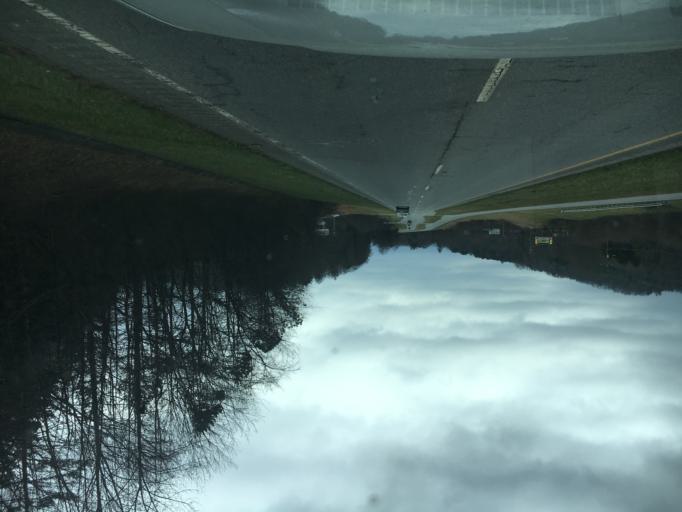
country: US
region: North Carolina
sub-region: Cherokee County
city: Murphy
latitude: 35.1521
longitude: -83.9620
